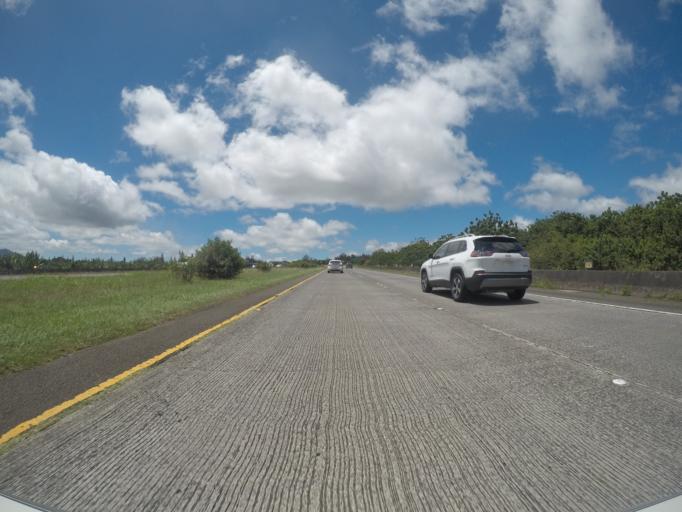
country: US
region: Hawaii
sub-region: Honolulu County
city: Wahiawa
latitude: 21.4847
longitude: -158.0252
